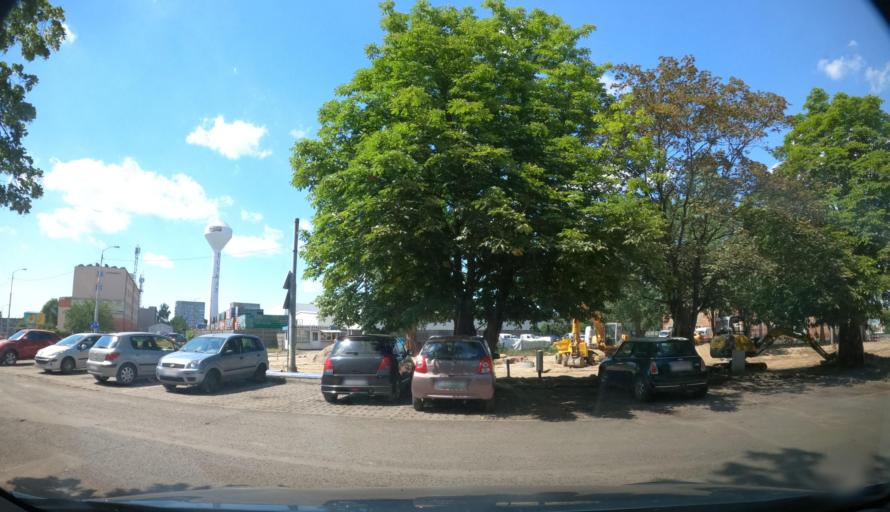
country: PL
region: West Pomeranian Voivodeship
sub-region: Szczecin
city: Szczecin
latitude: 53.4023
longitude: 14.5320
